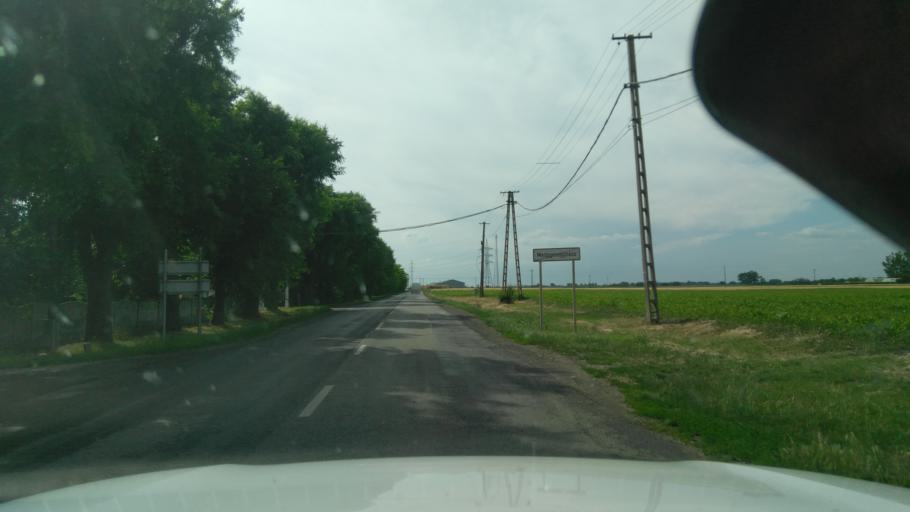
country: HU
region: Bekes
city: Medgyesegyhaza
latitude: 46.5036
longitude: 21.0160
